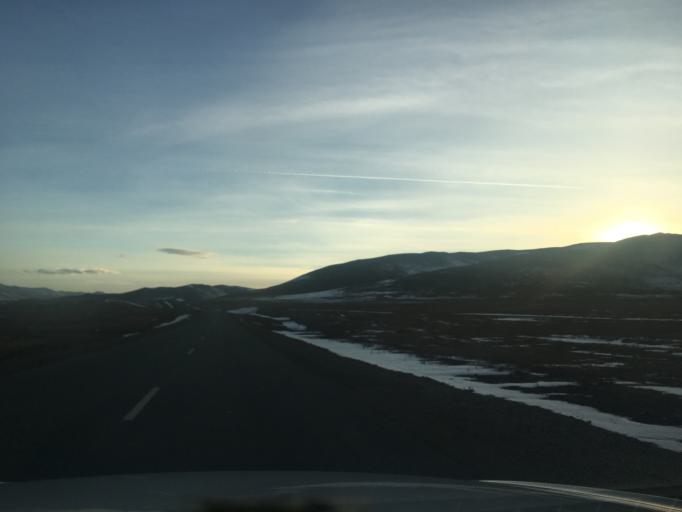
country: MN
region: Central Aimak
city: Mandal
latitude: 48.2301
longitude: 106.7186
